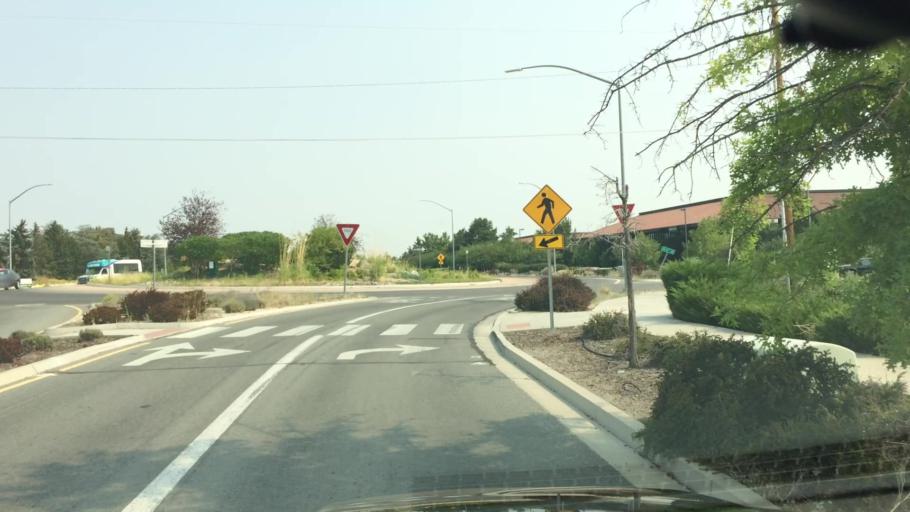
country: US
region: Nevada
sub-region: Washoe County
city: Reno
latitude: 39.4668
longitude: -119.7910
